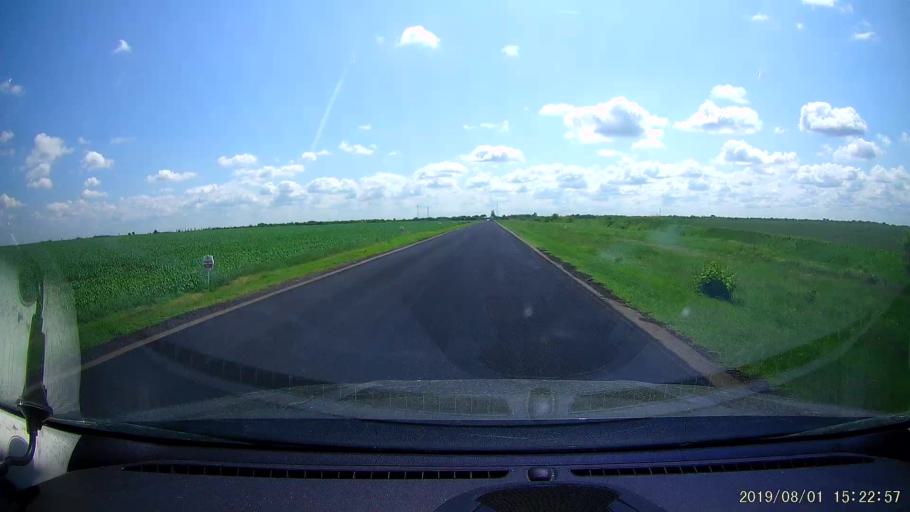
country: RO
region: Braila
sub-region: Comuna Viziru
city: Lanurile
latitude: 45.0470
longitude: 27.7678
